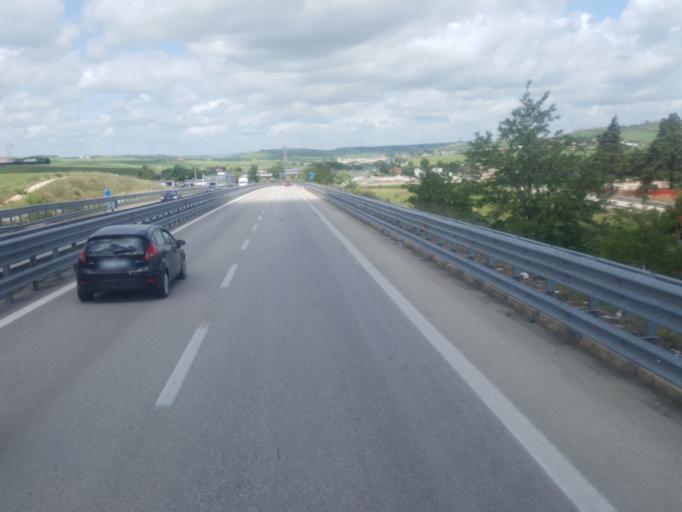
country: IT
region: Basilicate
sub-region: Provincia di Matera
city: Matera
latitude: 40.7050
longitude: 16.5844
